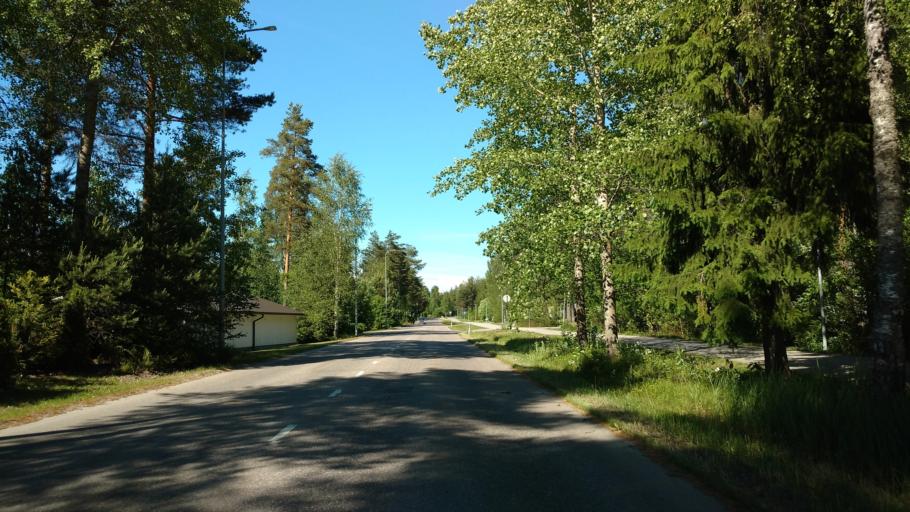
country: FI
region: Varsinais-Suomi
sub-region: Salo
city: Salo
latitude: 60.3916
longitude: 23.1853
